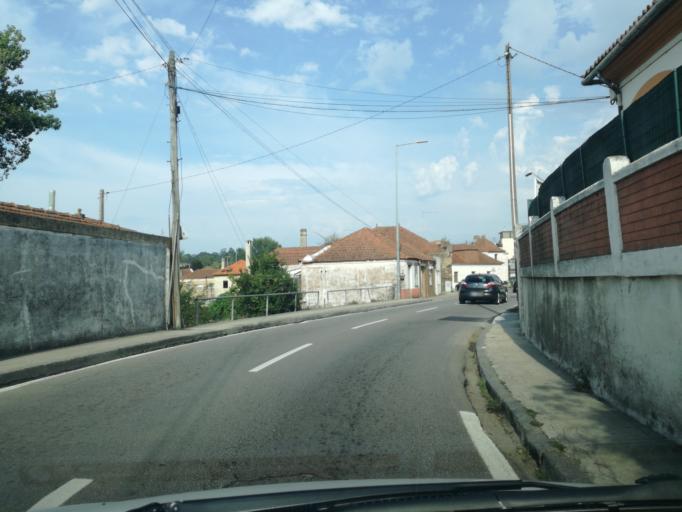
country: PT
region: Aveiro
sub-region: Espinho
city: Espinho
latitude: 41.0127
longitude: -8.6351
